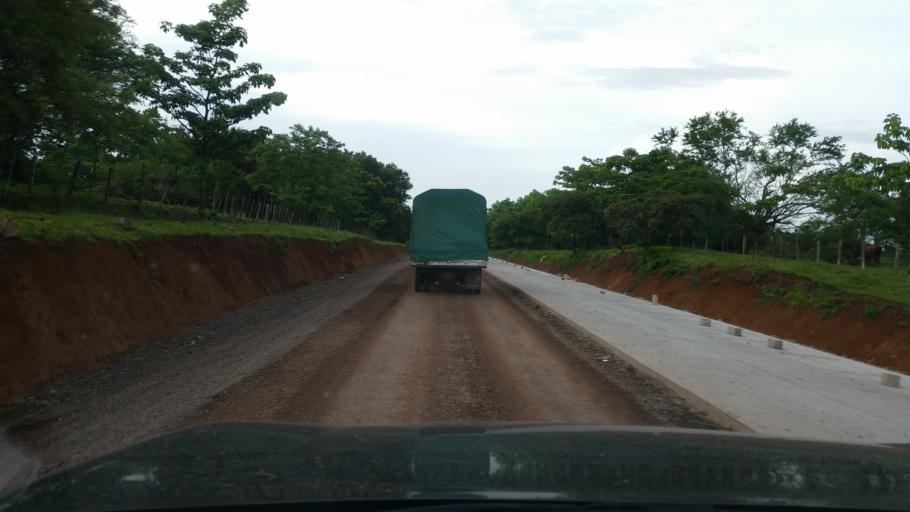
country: NI
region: Matagalpa
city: Rio Blanco
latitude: 13.2418
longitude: -84.9356
